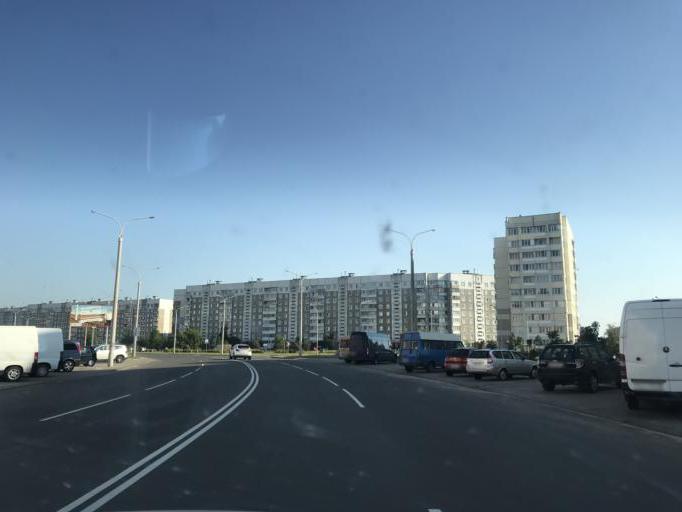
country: BY
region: Mogilev
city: Mahilyow
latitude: 53.8808
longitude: 30.3574
